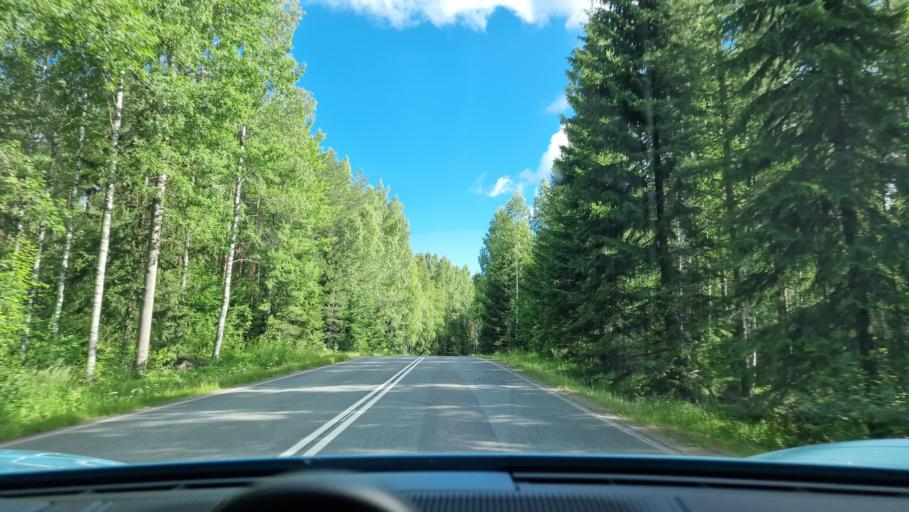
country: FI
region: Pirkanmaa
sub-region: Tampere
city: Paelkaene
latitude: 61.2629
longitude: 24.2369
